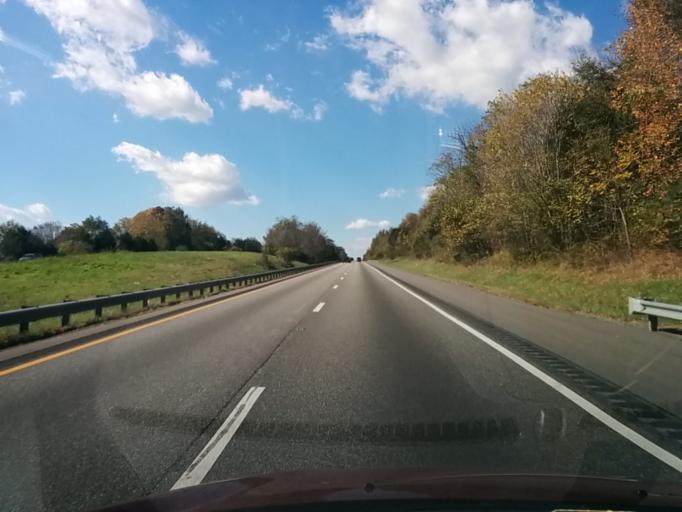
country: US
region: Virginia
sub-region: Botetourt County
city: Fincastle
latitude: 37.4642
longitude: -79.8204
